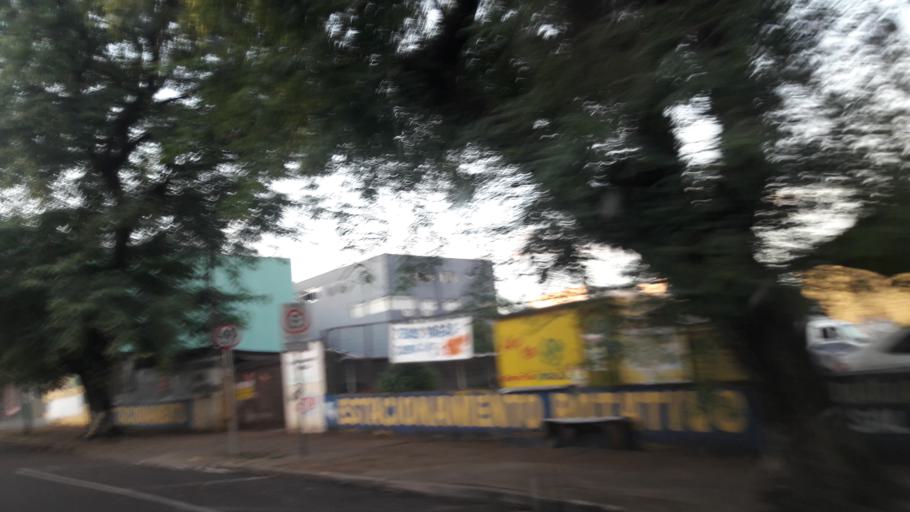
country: BR
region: Parana
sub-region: Cascavel
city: Cascavel
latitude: -24.9540
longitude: -53.4497
